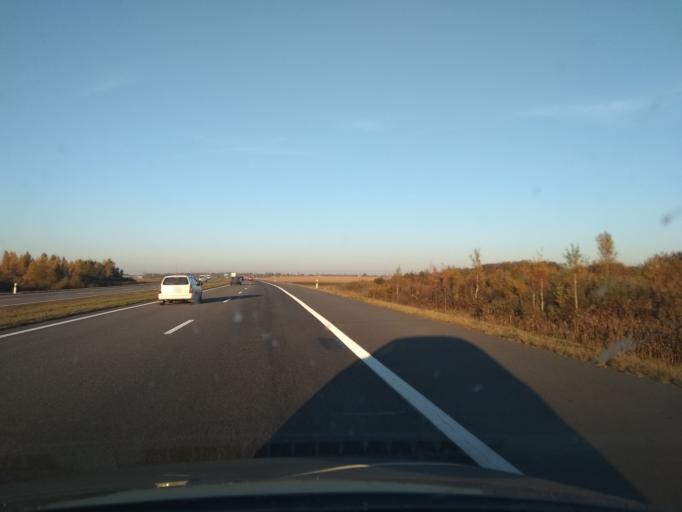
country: BY
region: Brest
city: Baranovichi
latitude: 53.1487
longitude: 25.9666
